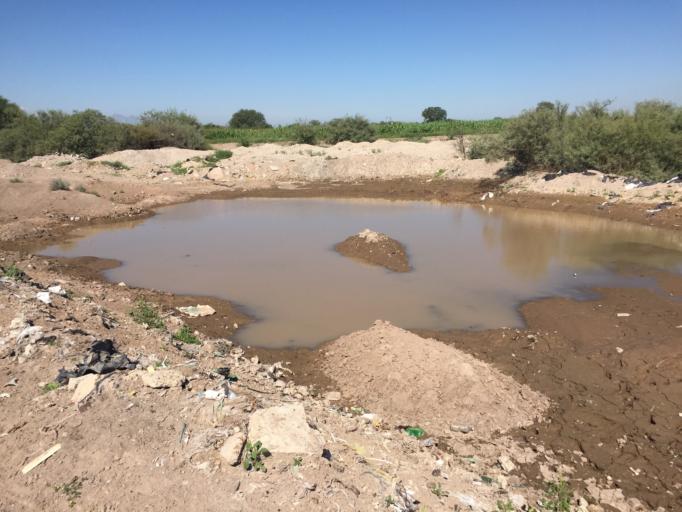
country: MX
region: Durango
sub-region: Gomez Palacio
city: San Felipe
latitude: 25.7287
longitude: -103.3736
